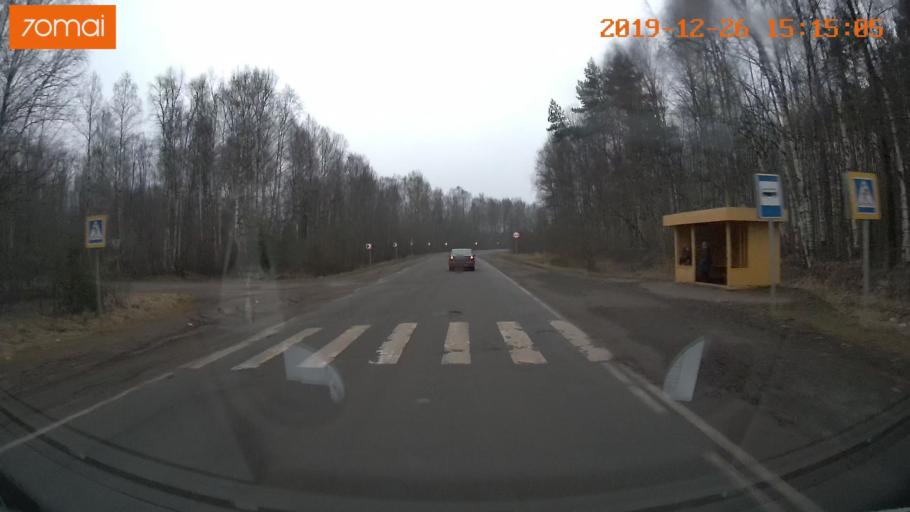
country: RU
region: Jaroslavl
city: Rybinsk
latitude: 58.1000
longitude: 38.8766
